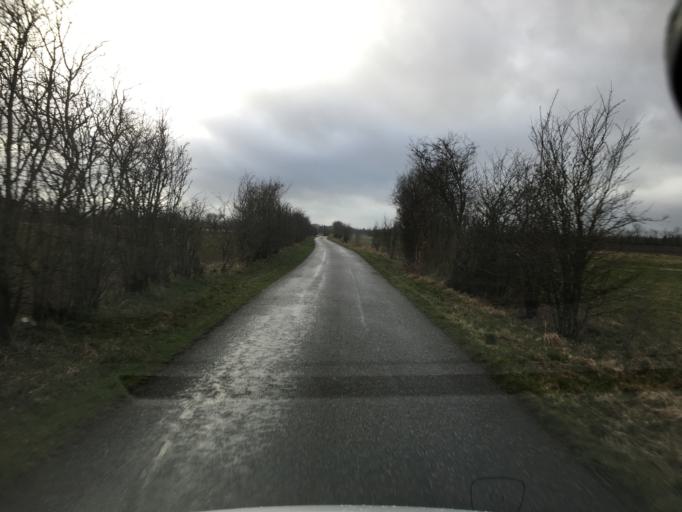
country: DE
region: Schleswig-Holstein
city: Bramstedtlund
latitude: 54.9463
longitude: 9.1228
